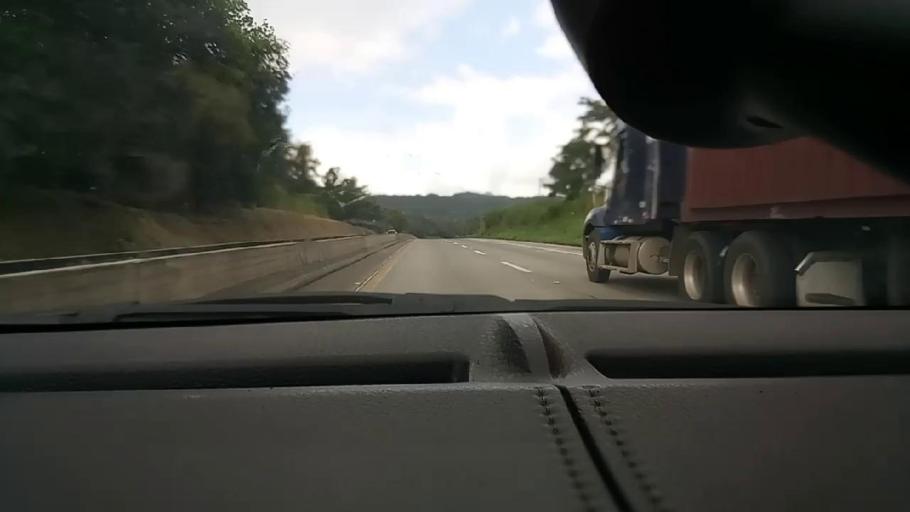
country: PA
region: Panama
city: Chilibre
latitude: 9.1467
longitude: -79.6310
